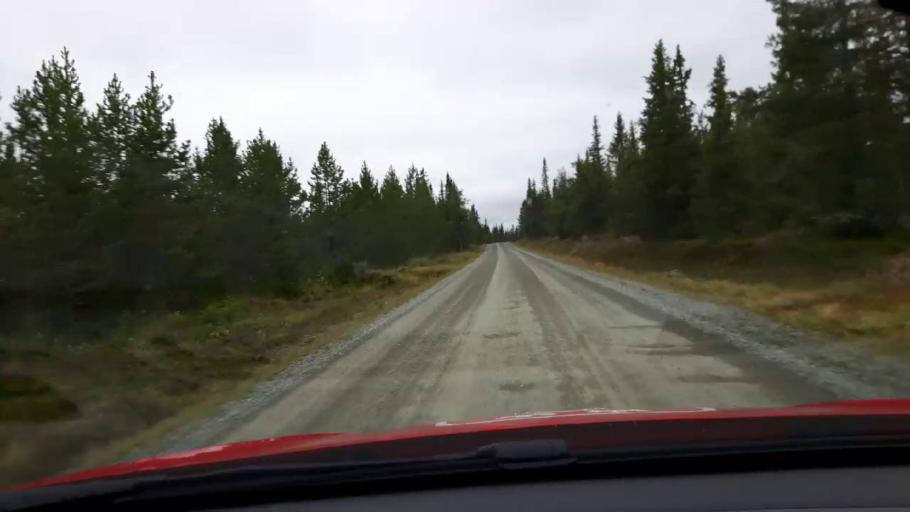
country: SE
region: Jaemtland
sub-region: Bergs Kommun
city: Hoverberg
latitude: 62.8754
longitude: 13.9694
